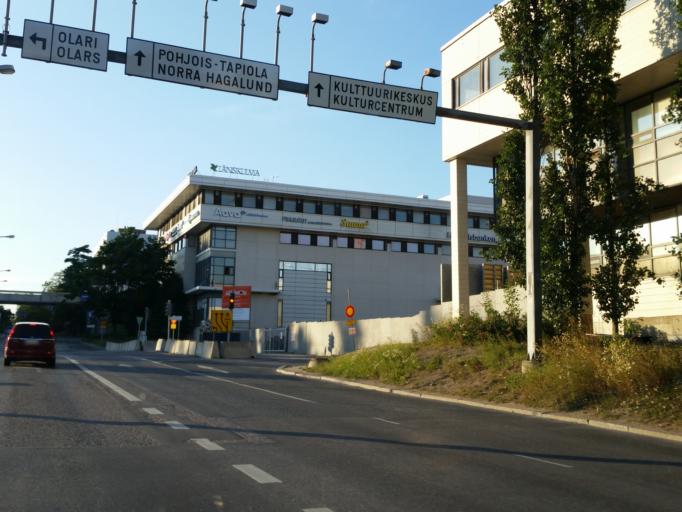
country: FI
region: Uusimaa
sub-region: Helsinki
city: Otaniemi
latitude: 60.1741
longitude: 24.8014
